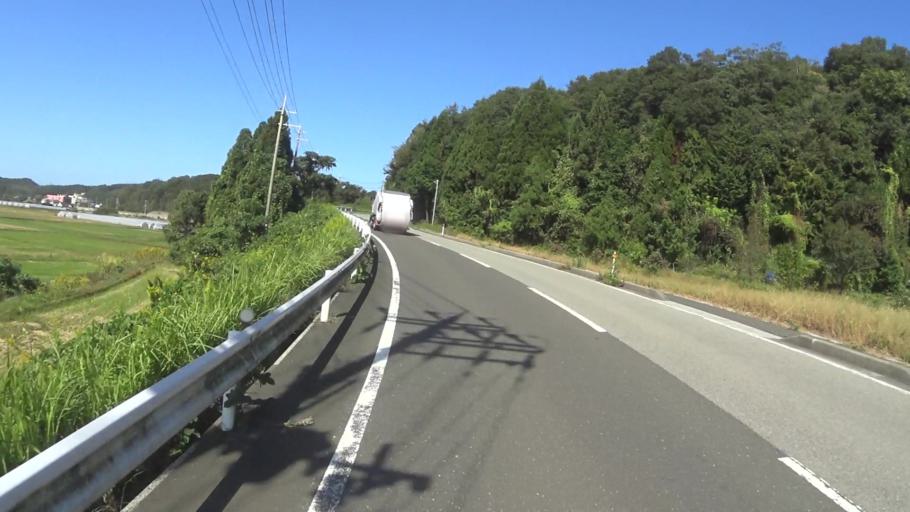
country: JP
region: Kyoto
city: Miyazu
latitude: 35.6919
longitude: 135.0508
